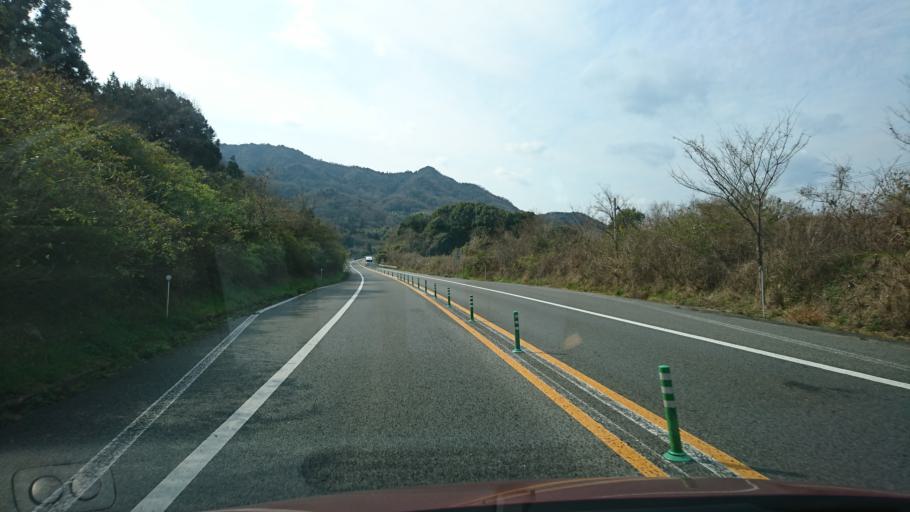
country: JP
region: Hiroshima
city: Innoshima
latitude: 34.1312
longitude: 133.0438
